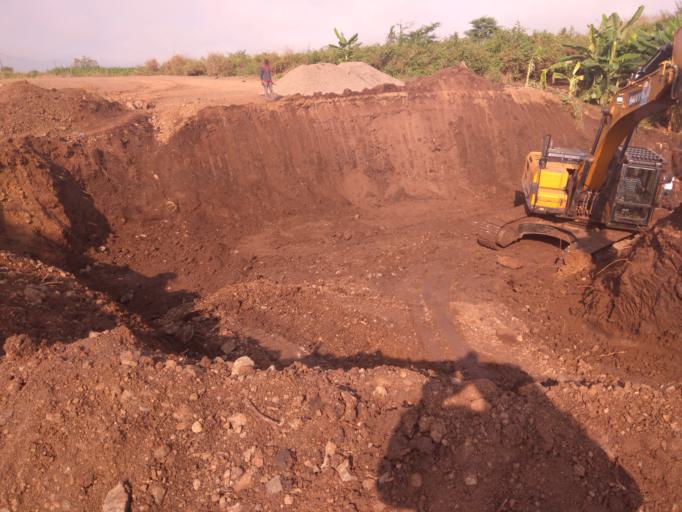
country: ET
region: Southern Nations, Nationalities, and People's Region
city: Felege Neway
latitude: 6.4144
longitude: 37.1640
